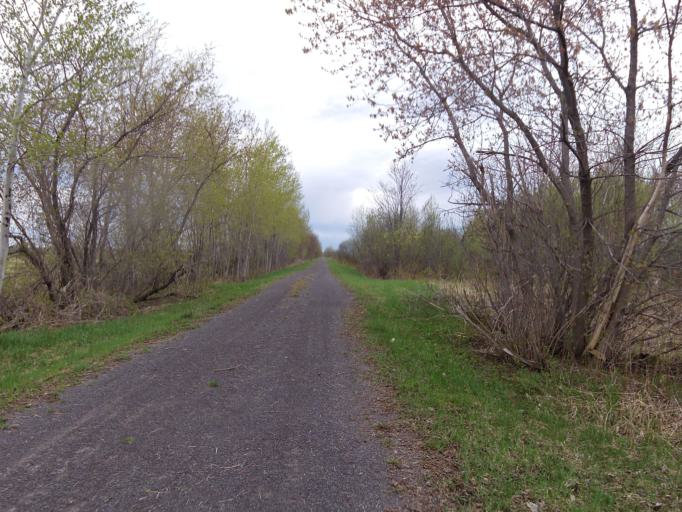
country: CA
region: Quebec
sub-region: Outaouais
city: Papineauville
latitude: 45.5261
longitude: -74.9016
